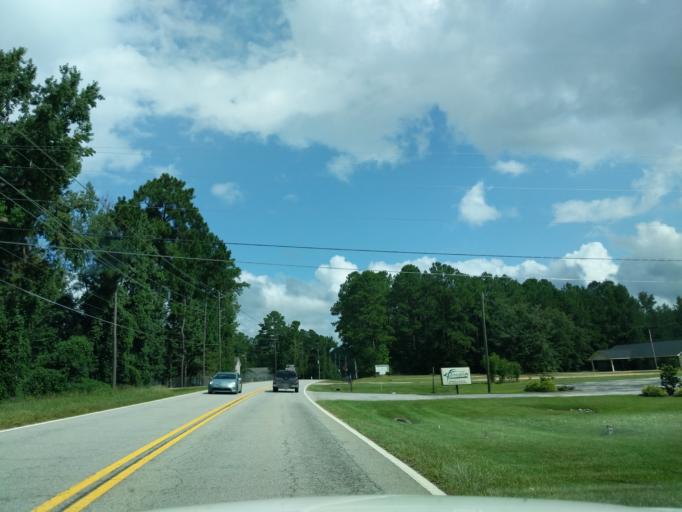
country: US
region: Georgia
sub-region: Columbia County
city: Evans
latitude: 33.5538
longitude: -82.1624
